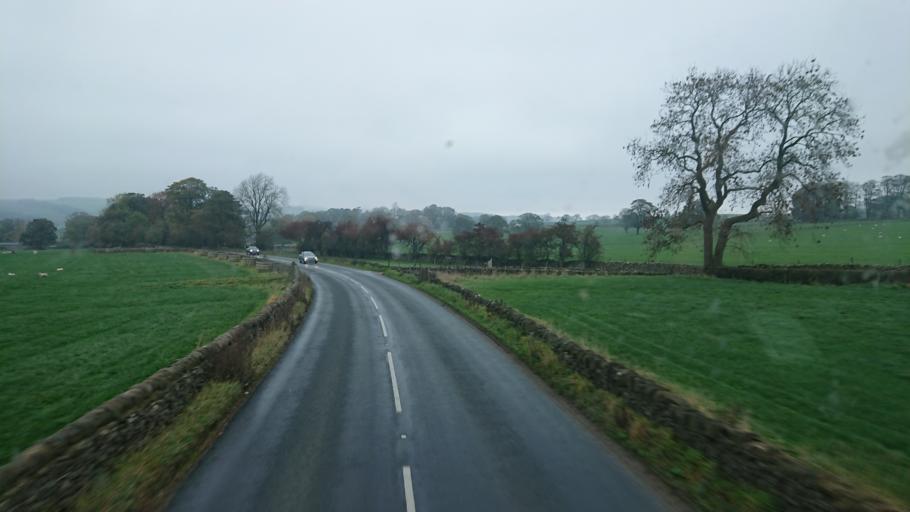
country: GB
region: England
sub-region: North Yorkshire
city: Skipton
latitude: 54.0194
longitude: -2.0451
